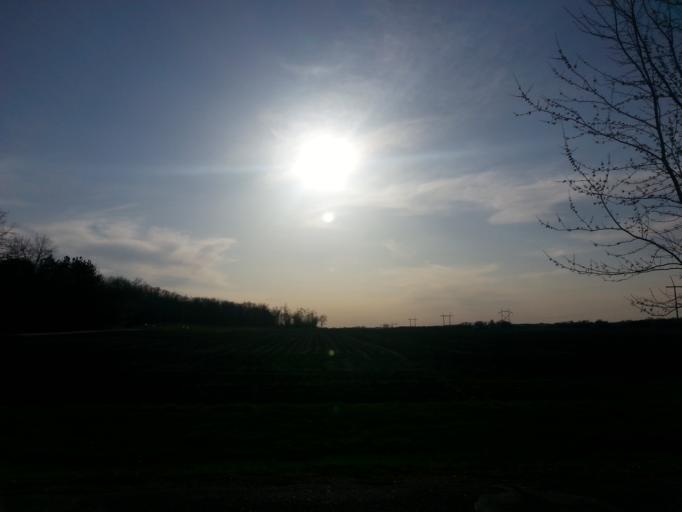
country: US
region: Minnesota
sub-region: Washington County
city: Afton
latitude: 44.8539
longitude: -92.7159
